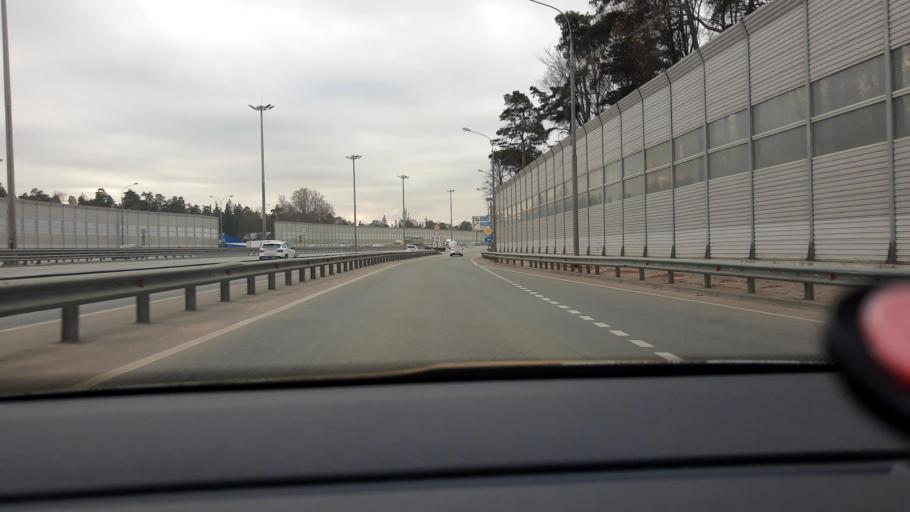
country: RU
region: Moskovskaya
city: Bolshevo
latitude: 55.9386
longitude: 37.8117
